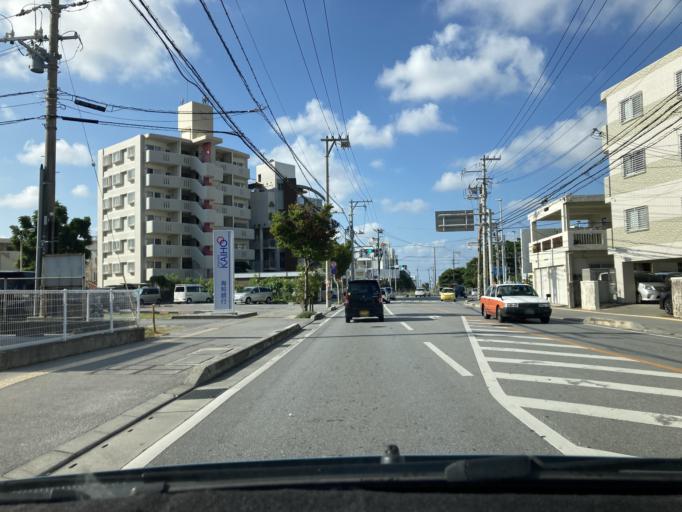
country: JP
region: Okinawa
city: Naha-shi
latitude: 26.2281
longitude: 127.7201
